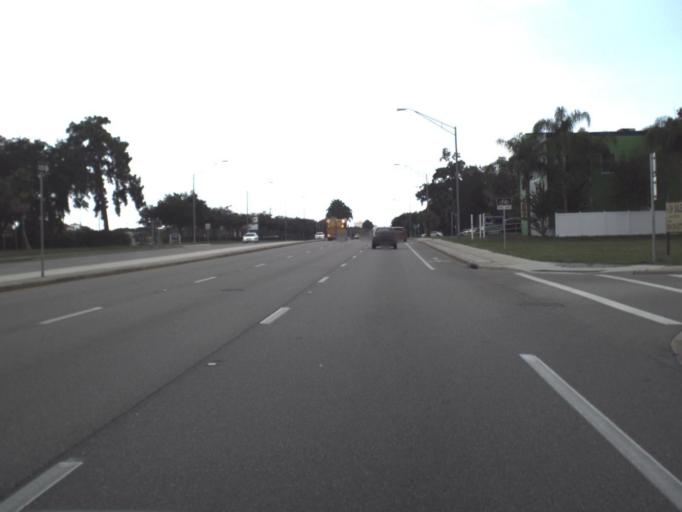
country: US
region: Florida
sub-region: Sarasota County
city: Kensington Park
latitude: 27.3376
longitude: -82.5066
